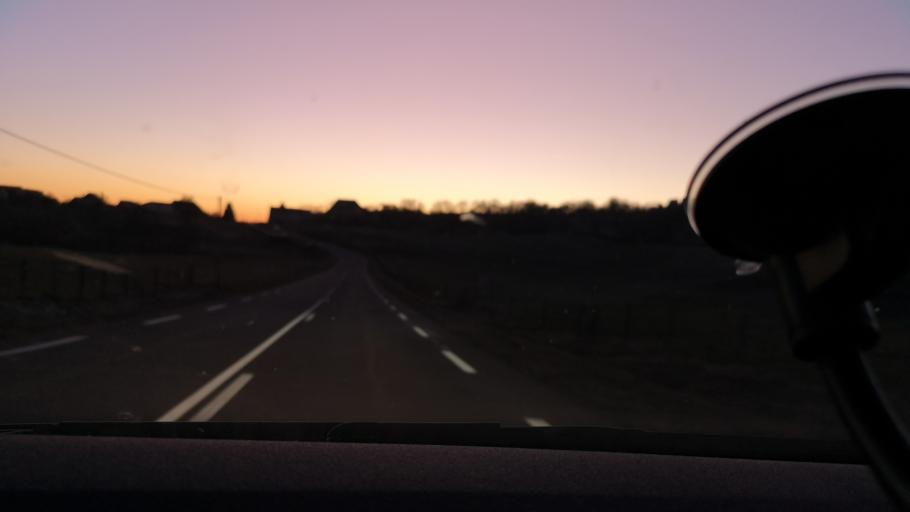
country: FR
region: Franche-Comte
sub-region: Departement du Jura
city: Champagnole
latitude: 46.7993
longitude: 6.0145
